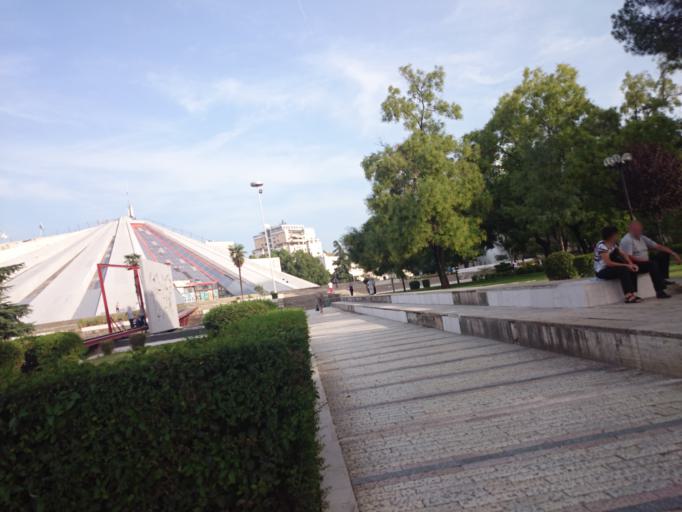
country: AL
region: Tirane
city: Tirana
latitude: 41.3234
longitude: 19.8200
